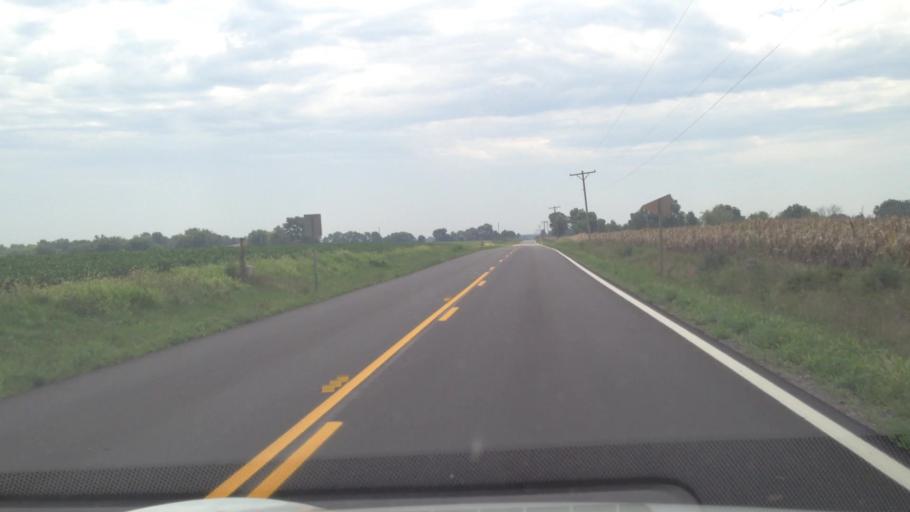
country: US
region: Kansas
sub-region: Crawford County
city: Girard
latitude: 37.6335
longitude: -94.9698
